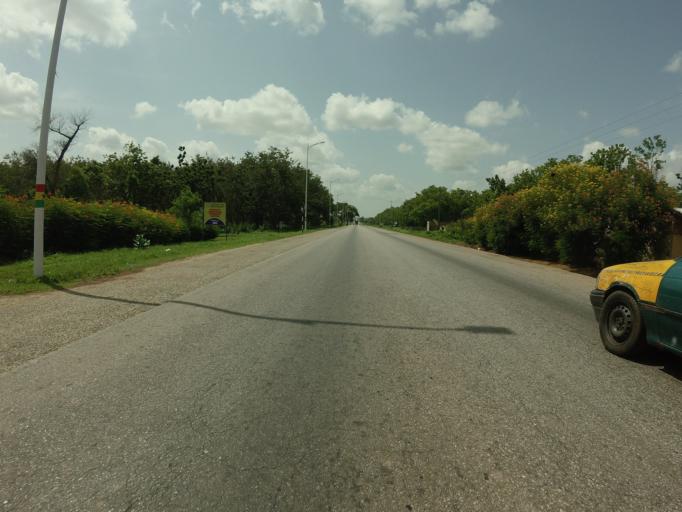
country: GH
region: Northern
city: Savelugu
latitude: 9.5373
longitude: -0.8395
